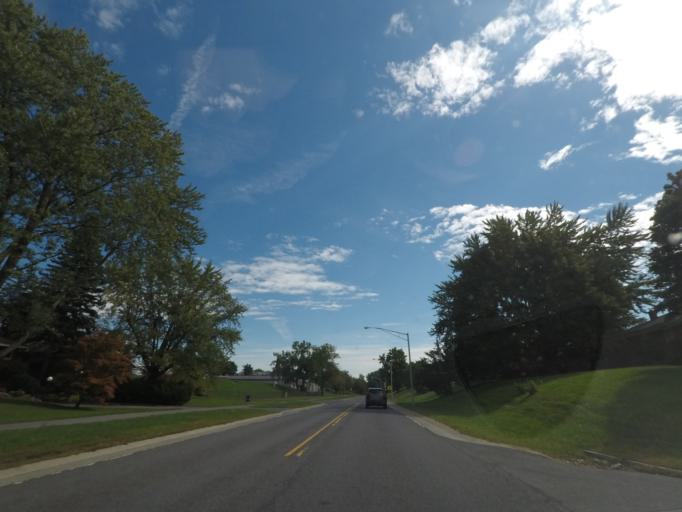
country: US
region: New York
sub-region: Albany County
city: Albany
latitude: 42.6472
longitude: -73.7920
